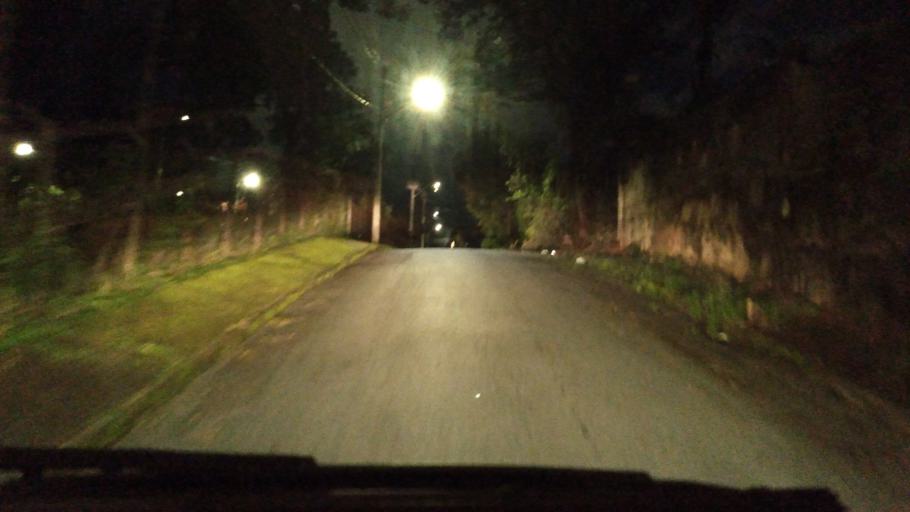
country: BR
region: Minas Gerais
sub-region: Belo Horizonte
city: Belo Horizonte
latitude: -19.8958
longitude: -43.9733
